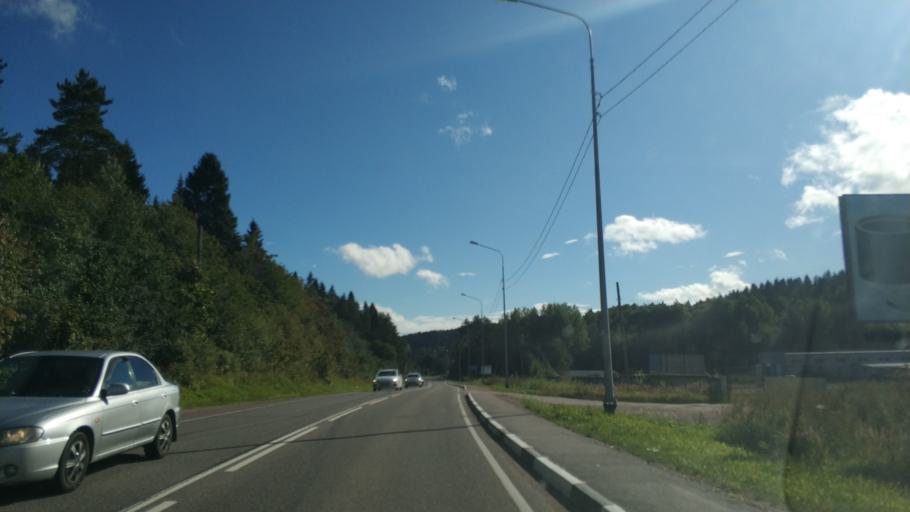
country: RU
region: Republic of Karelia
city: Sortavala
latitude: 61.6755
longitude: 30.6552
